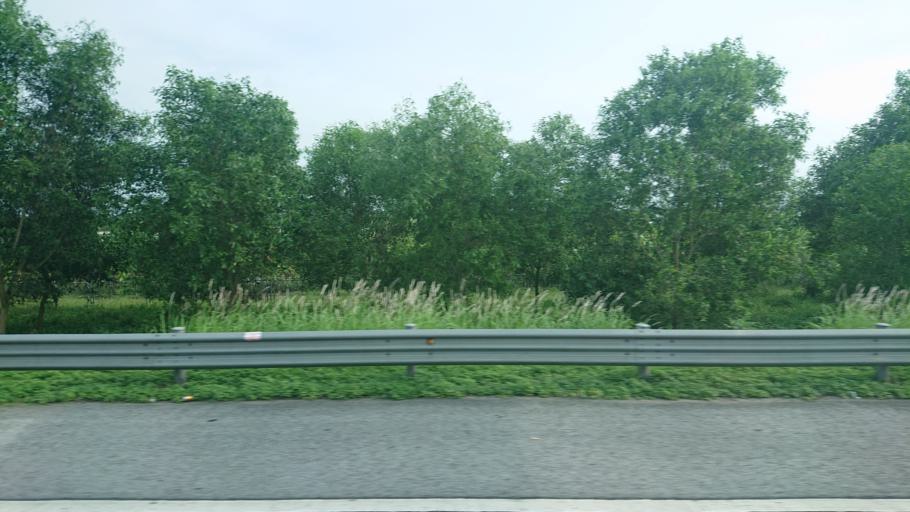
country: VN
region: Hai Phong
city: An Lao
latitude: 20.8005
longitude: 106.5328
